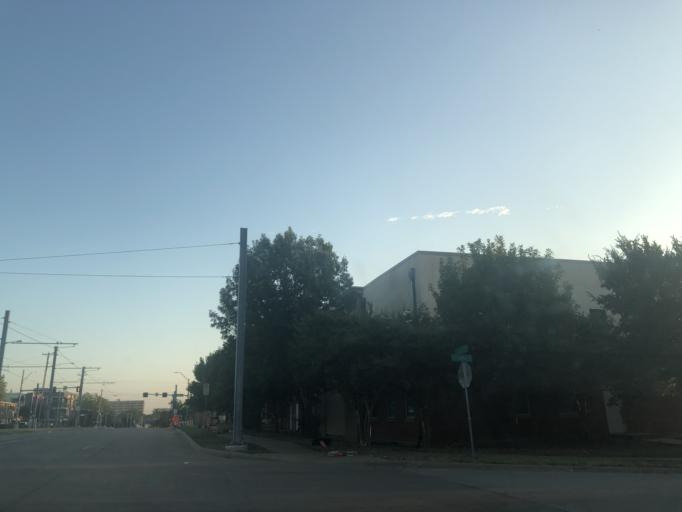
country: US
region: Texas
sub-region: Dallas County
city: Dallas
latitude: 32.7521
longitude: -96.8240
